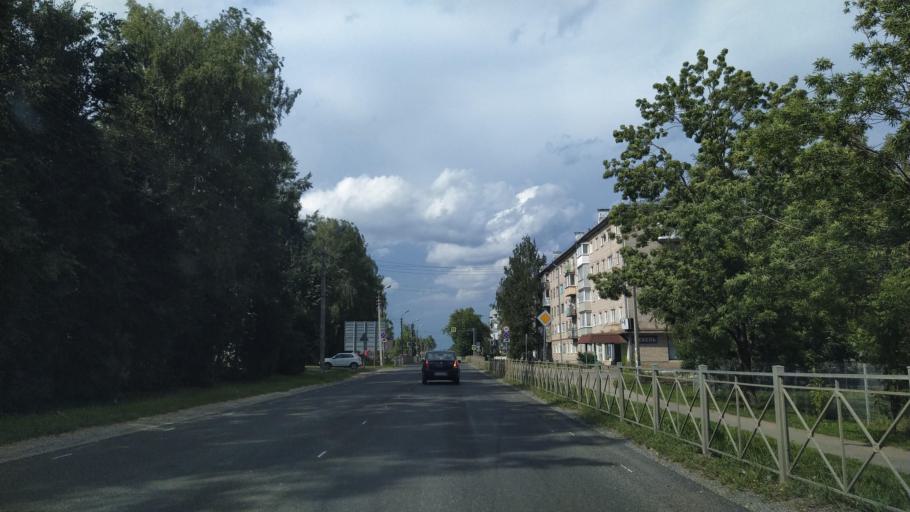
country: RU
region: Pskov
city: Porkhov
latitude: 57.7615
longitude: 29.5567
